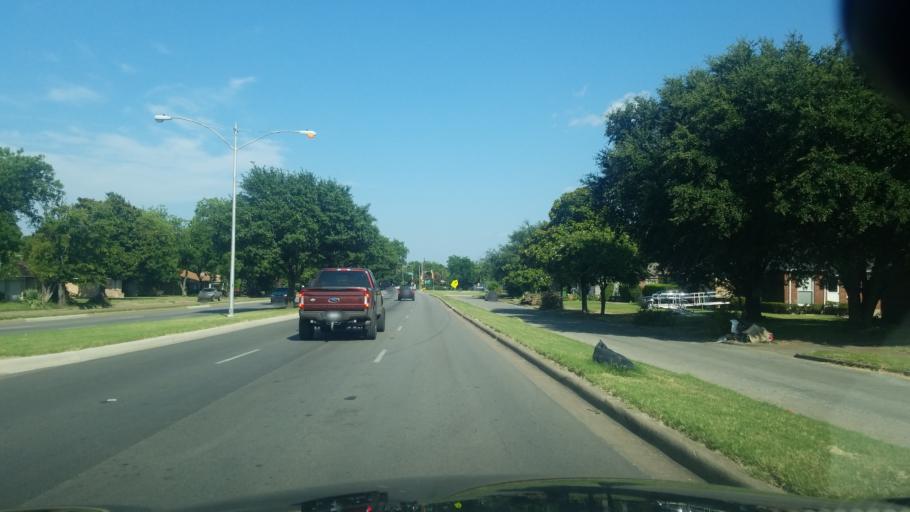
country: US
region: Texas
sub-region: Dallas County
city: Dallas
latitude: 32.7183
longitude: -96.7881
